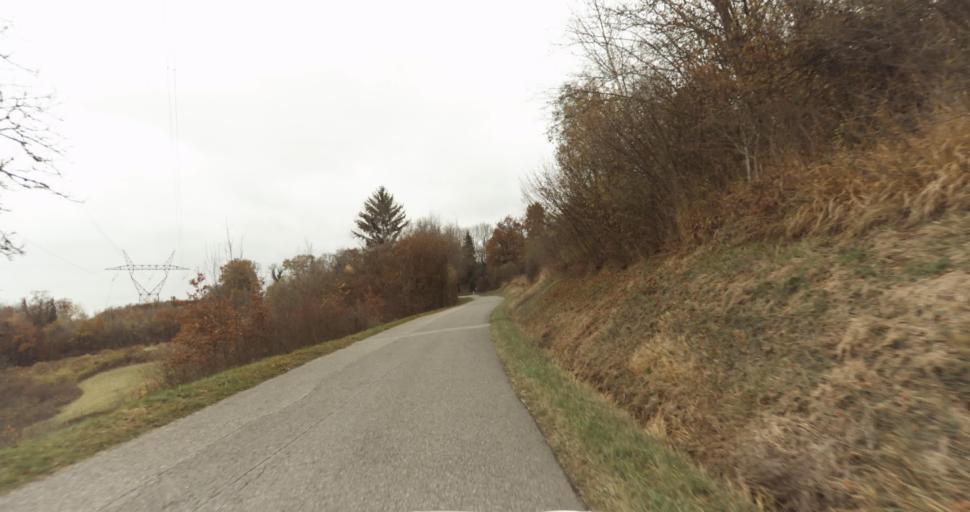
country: FR
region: Rhone-Alpes
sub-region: Departement de la Haute-Savoie
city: Chavanod
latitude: 45.8776
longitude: 6.0379
